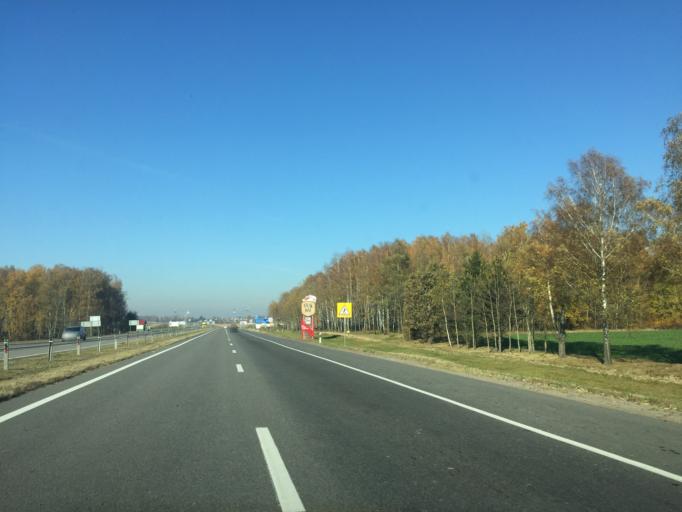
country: BY
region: Mogilev
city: Buynichy
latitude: 53.9539
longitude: 30.2117
